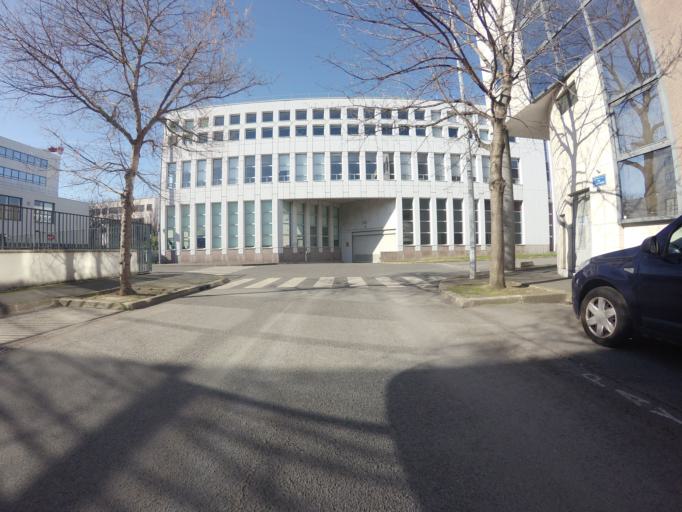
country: FR
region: Ile-de-France
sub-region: Departement des Hauts-de-Seine
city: Clichy
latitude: 48.9068
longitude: 2.3172
